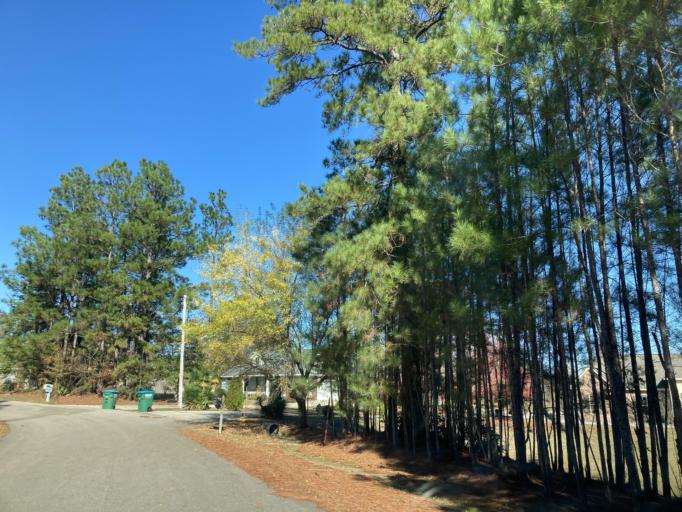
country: US
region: Mississippi
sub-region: Forrest County
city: Petal
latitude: 31.3531
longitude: -89.1988
